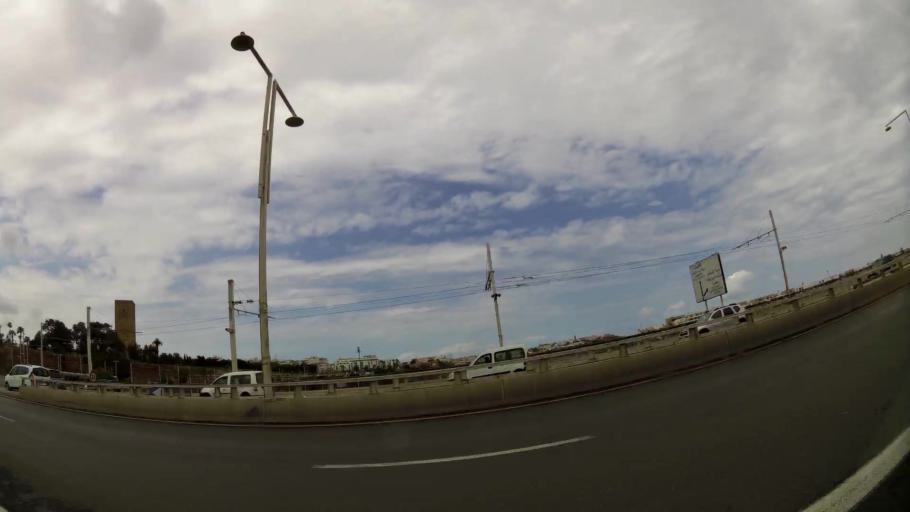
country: MA
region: Rabat-Sale-Zemmour-Zaer
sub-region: Rabat
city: Rabat
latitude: 34.0261
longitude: -6.8194
